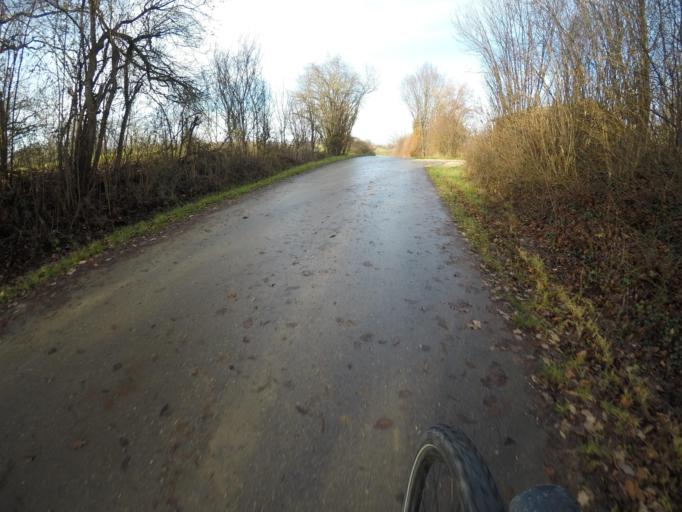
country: DE
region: Baden-Wuerttemberg
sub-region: Regierungsbezirk Stuttgart
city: Dettingen unter Teck
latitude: 48.6198
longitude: 9.4427
